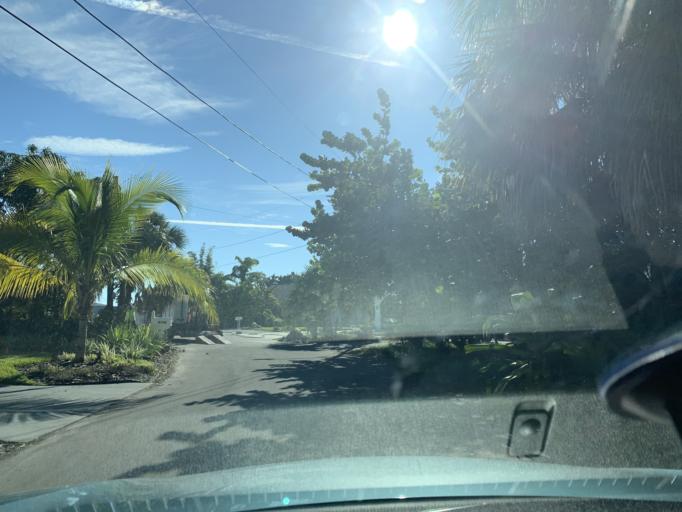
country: US
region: Florida
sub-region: Pinellas County
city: Gulfport
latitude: 27.7387
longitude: -82.6990
